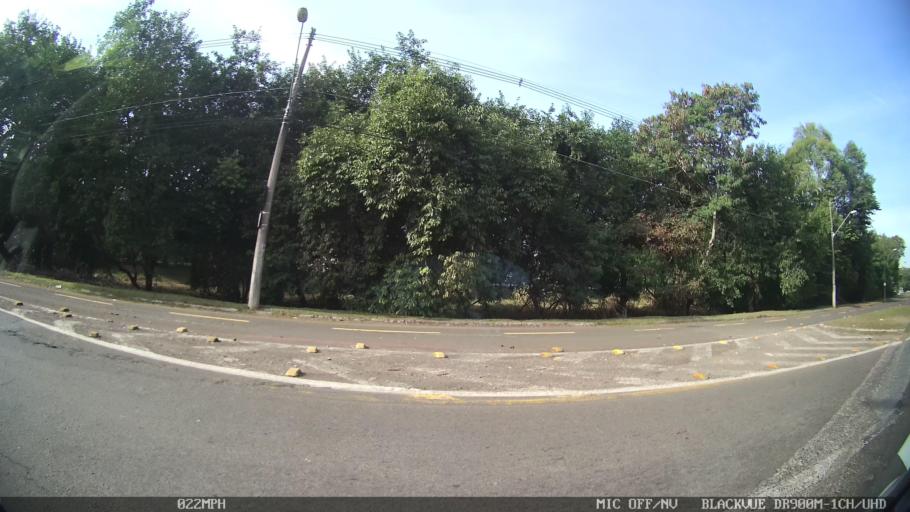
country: BR
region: Sao Paulo
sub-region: Piracicaba
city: Piracicaba
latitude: -22.7250
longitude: -47.6713
